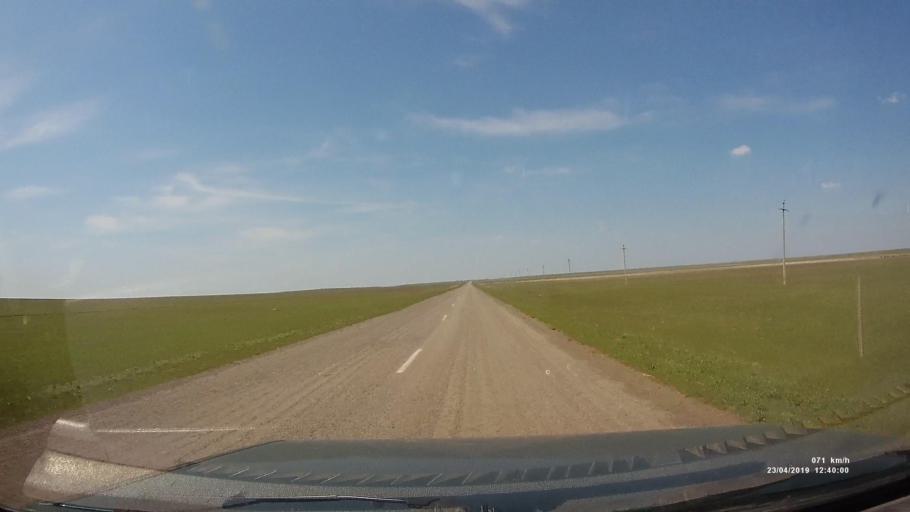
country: RU
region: Kalmykiya
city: Yashalta
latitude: 46.4373
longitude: 42.7026
